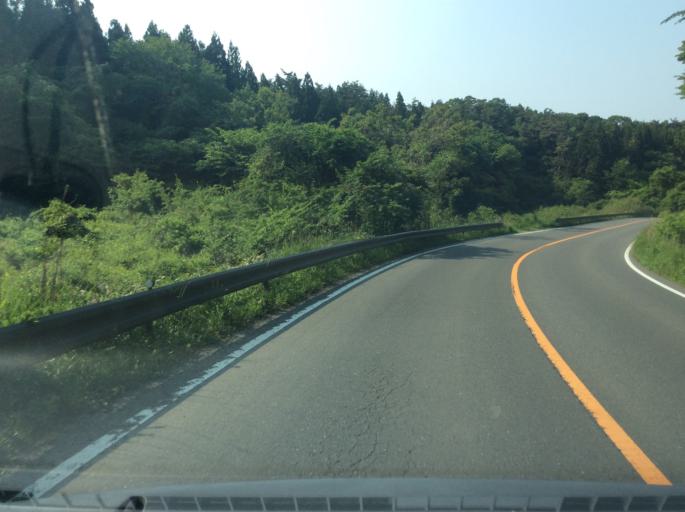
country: JP
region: Tochigi
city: Kuroiso
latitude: 37.0893
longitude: 140.2229
